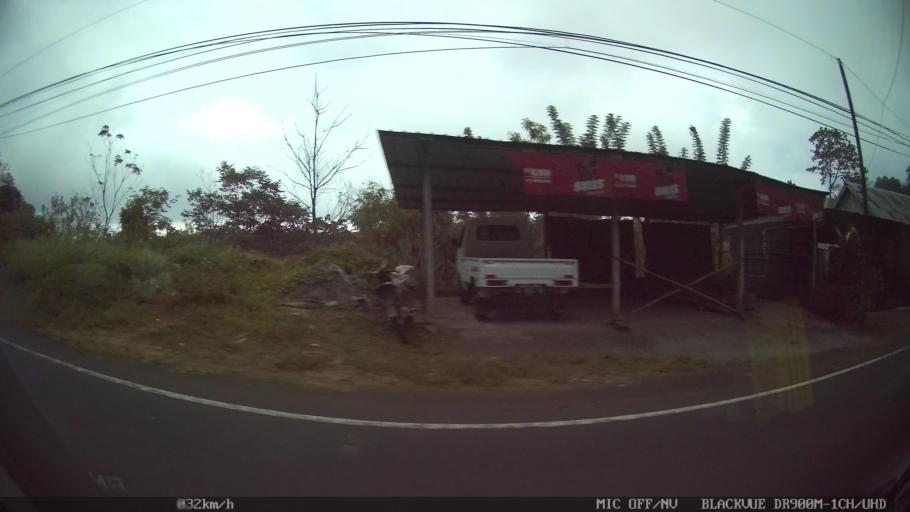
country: ID
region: Bali
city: Klau
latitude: -8.3331
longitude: 115.0320
